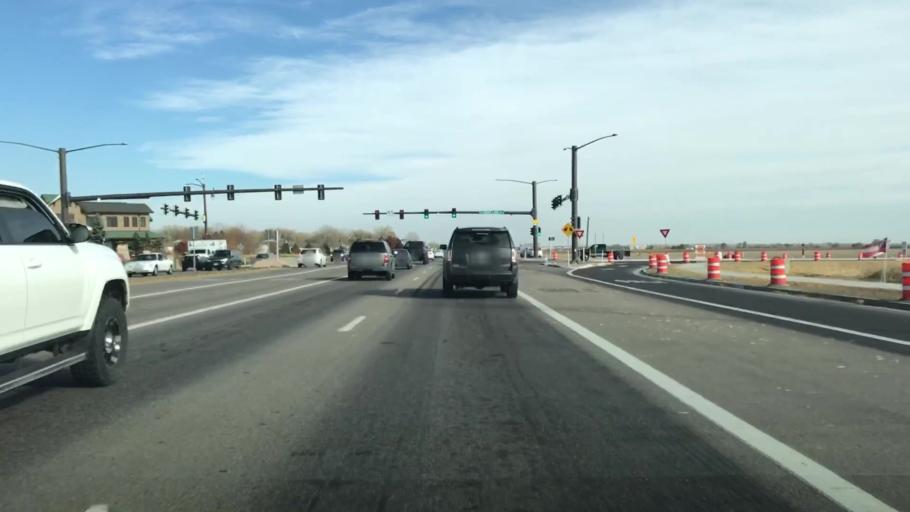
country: US
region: Colorado
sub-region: Larimer County
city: Loveland
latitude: 40.4072
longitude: -105.0221
